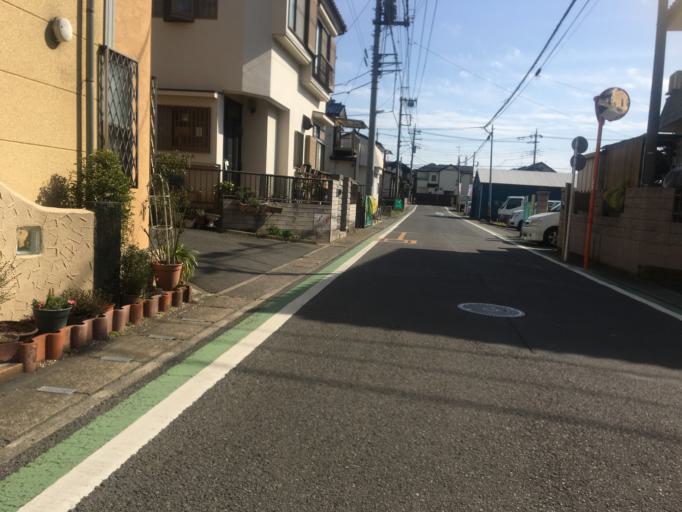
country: JP
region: Saitama
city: Shiki
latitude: 35.8337
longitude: 139.5944
